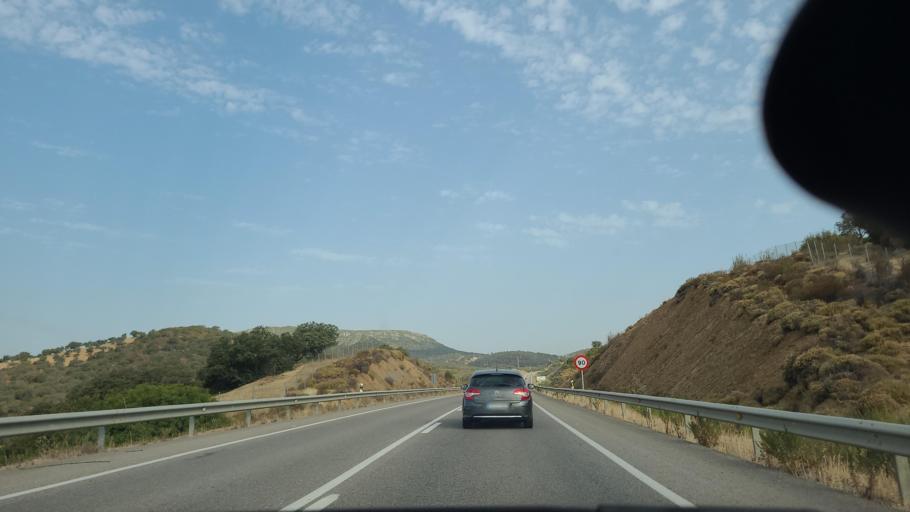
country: ES
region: Andalusia
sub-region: Province of Cordoba
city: Espiel
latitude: 38.1501
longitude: -4.9763
